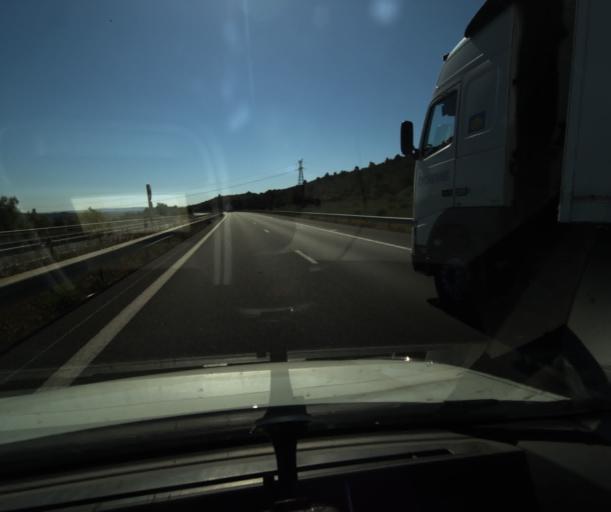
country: FR
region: Languedoc-Roussillon
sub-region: Departement de l'Aude
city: Puicheric
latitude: 43.1739
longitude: 2.6501
